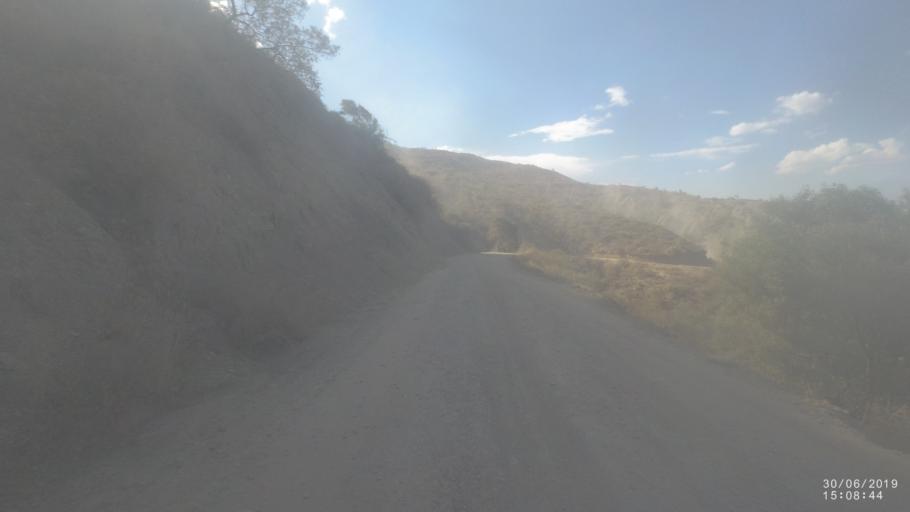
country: BO
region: Cochabamba
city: Irpa Irpa
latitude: -17.7310
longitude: -66.3010
